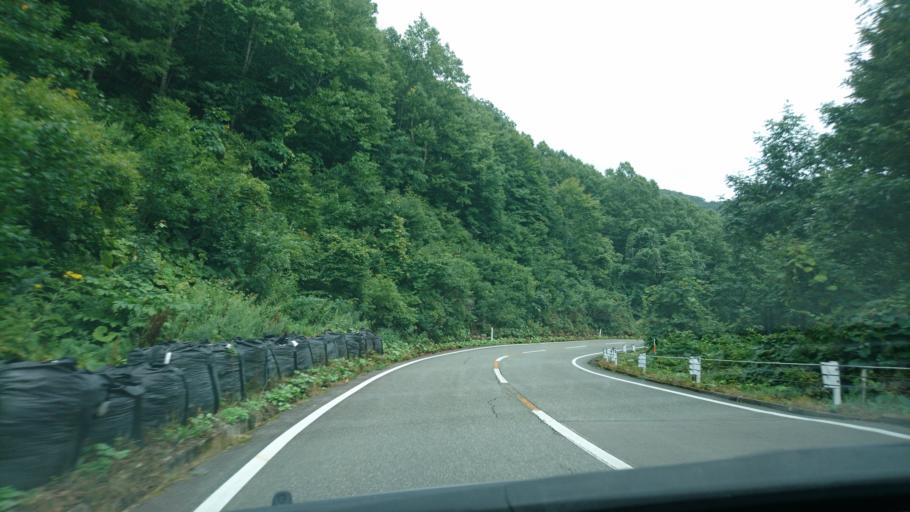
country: JP
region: Akita
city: Yuzawa
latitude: 38.9782
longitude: 140.7205
